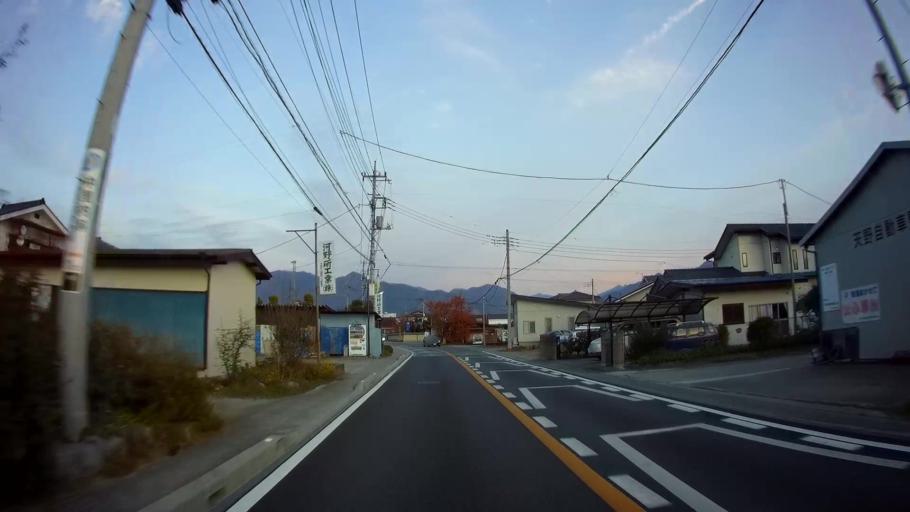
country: JP
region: Yamanashi
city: Enzan
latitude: 35.6650
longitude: 138.6958
